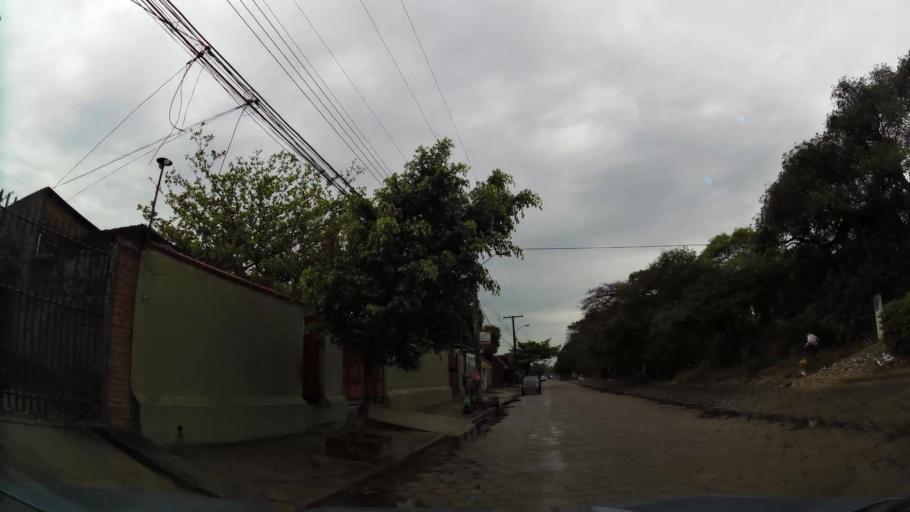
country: BO
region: Santa Cruz
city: Santa Cruz de la Sierra
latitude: -17.8098
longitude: -63.1988
